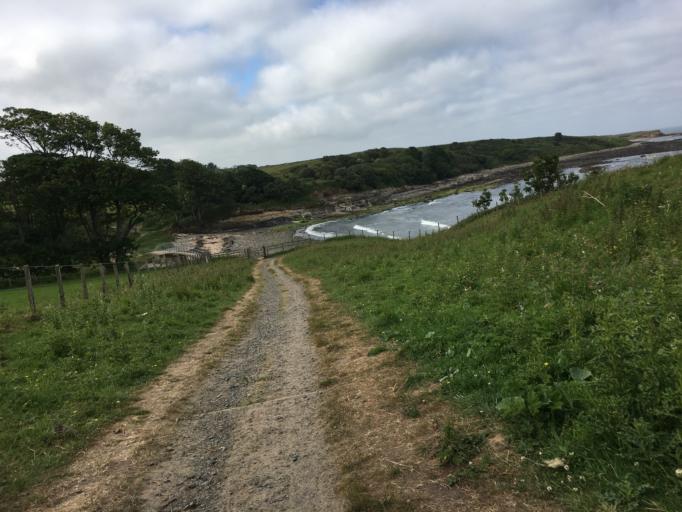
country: GB
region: England
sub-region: Northumberland
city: Alnmouth
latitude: 55.4392
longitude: -1.5929
